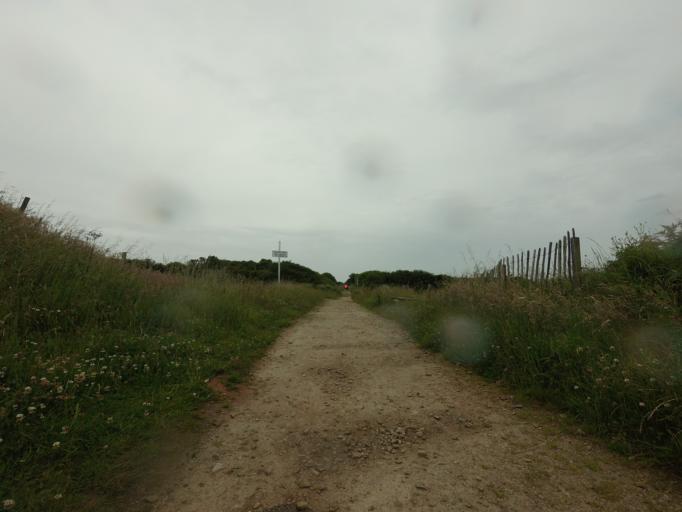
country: GB
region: Scotland
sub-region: Moray
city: Portknockie
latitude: 57.6976
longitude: -2.8503
